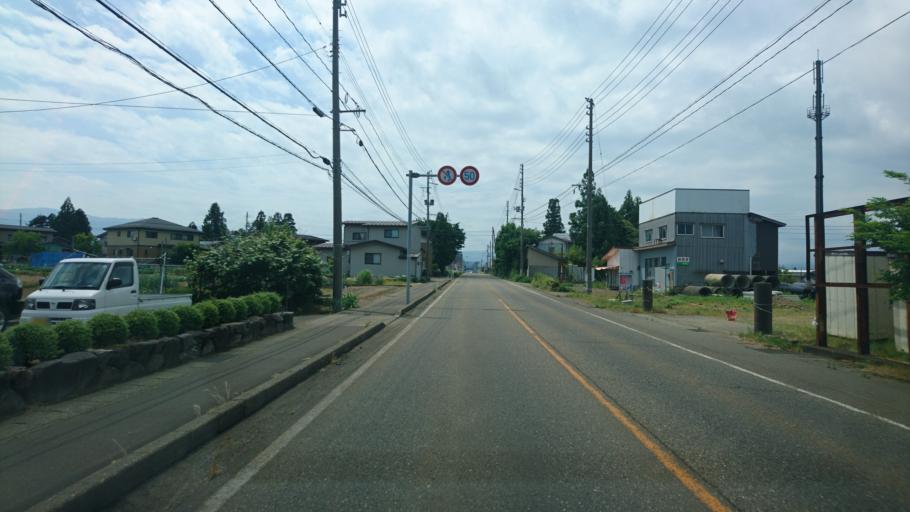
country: JP
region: Niigata
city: Arai
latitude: 37.0693
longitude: 138.2574
